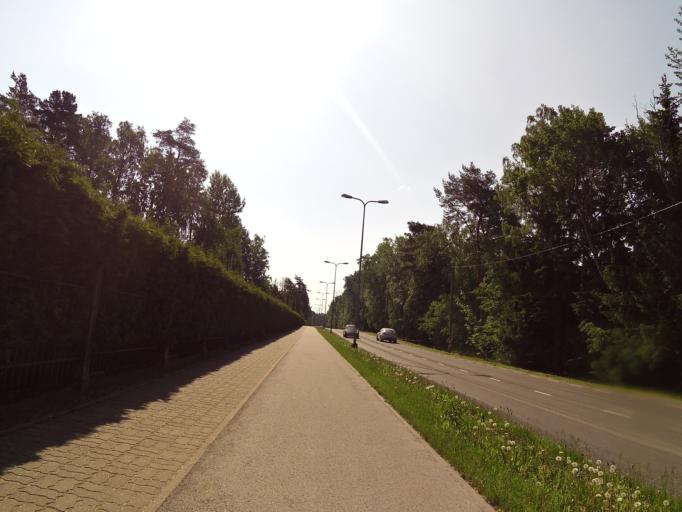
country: EE
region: Harju
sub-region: Harku vald
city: Tabasalu
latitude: 59.4445
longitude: 24.6133
